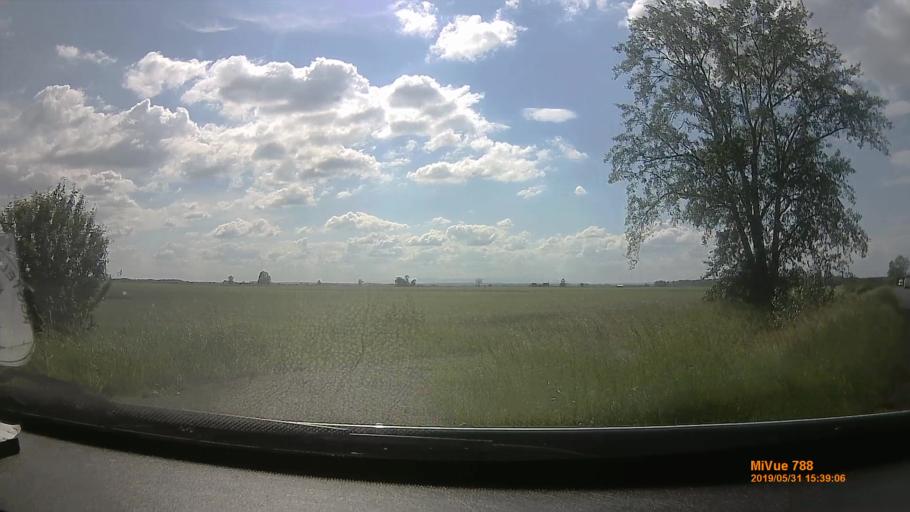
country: HU
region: Borsod-Abauj-Zemplen
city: Prugy
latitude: 48.1053
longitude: 21.2312
